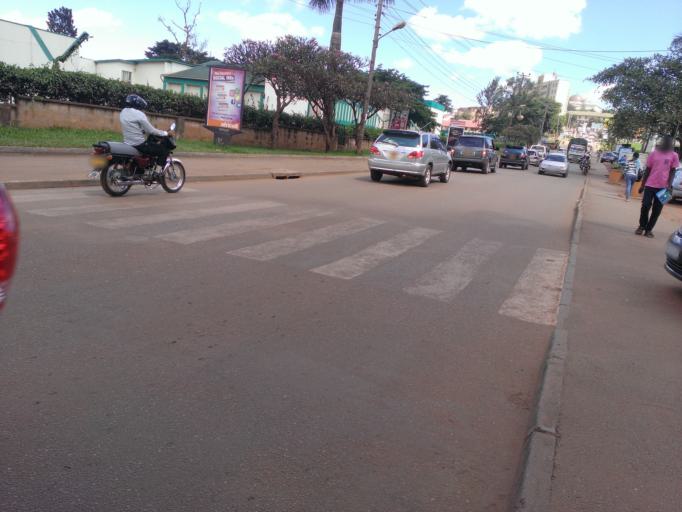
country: UG
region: Central Region
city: Kampala Central Division
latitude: 0.3217
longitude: 32.5693
